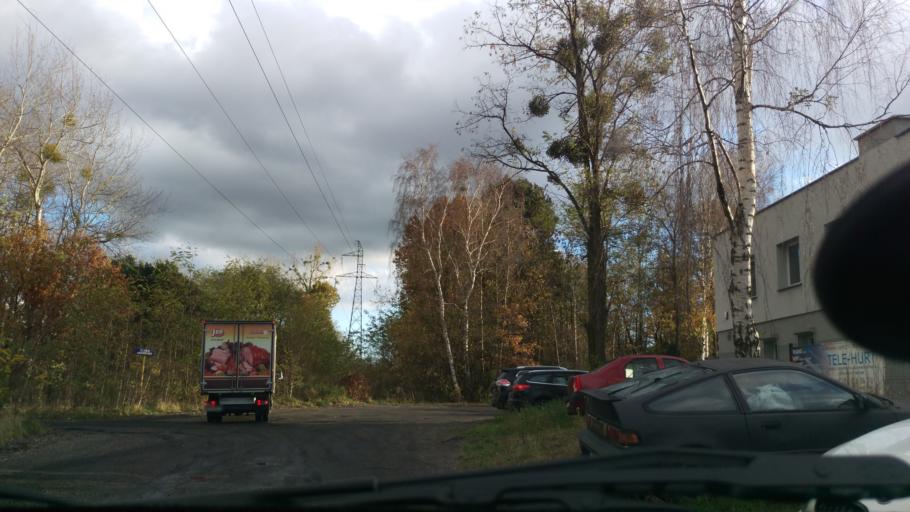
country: PL
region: West Pomeranian Voivodeship
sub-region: Powiat gryfinski
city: Stare Czarnowo
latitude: 53.3709
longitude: 14.6788
